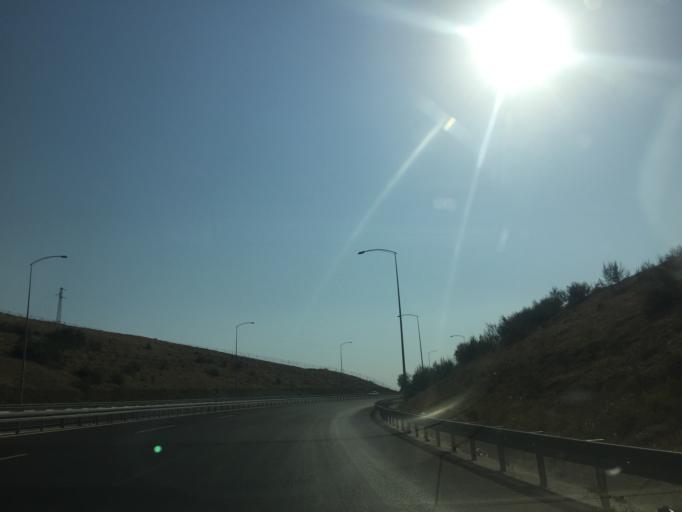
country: TR
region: Manisa
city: Karaoglanli
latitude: 38.5028
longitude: 27.5989
